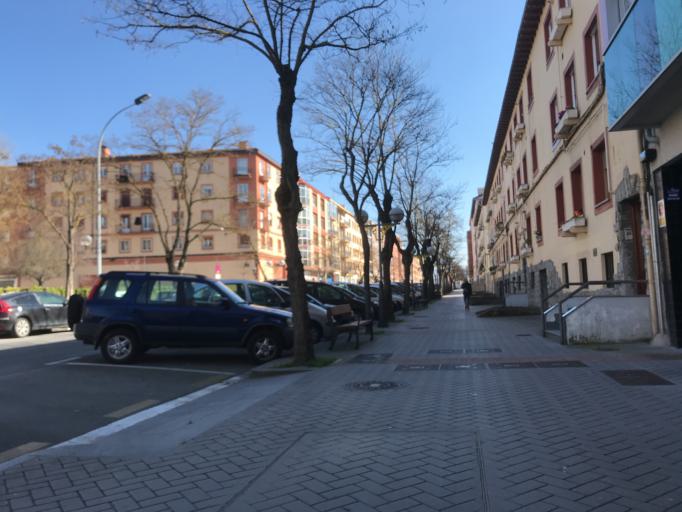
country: ES
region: Basque Country
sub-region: Provincia de Alava
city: Gasteiz / Vitoria
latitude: 42.8378
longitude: -2.6645
